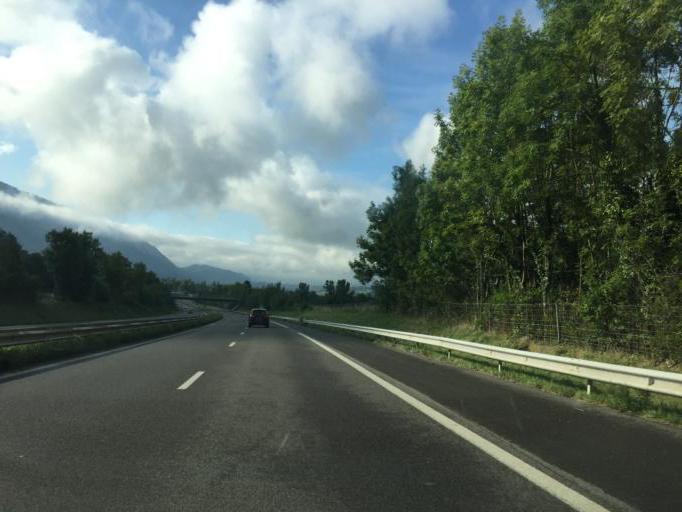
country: FR
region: Rhone-Alpes
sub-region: Departement de la Savoie
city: Drumettaz-Clarafond
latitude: 45.6673
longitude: 5.9251
